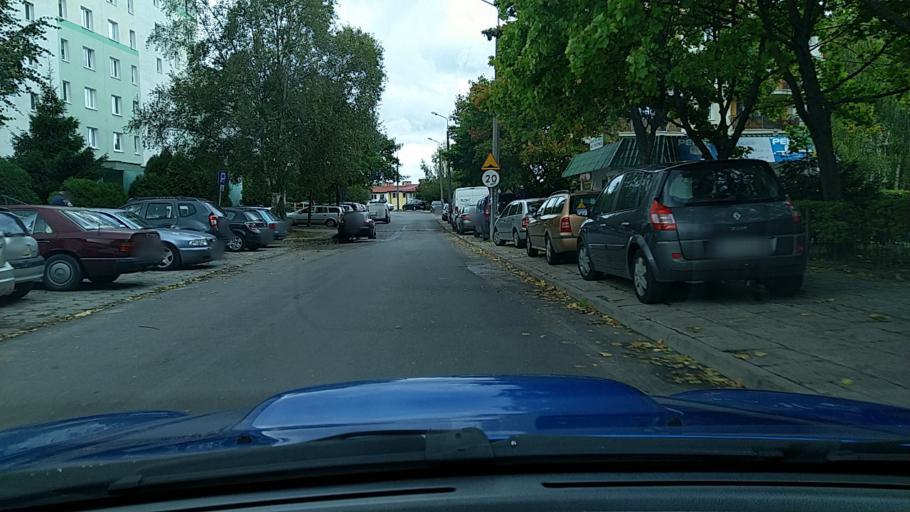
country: PL
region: Warmian-Masurian Voivodeship
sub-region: Olsztyn
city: Kortowo
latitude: 53.7419
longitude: 20.4812
